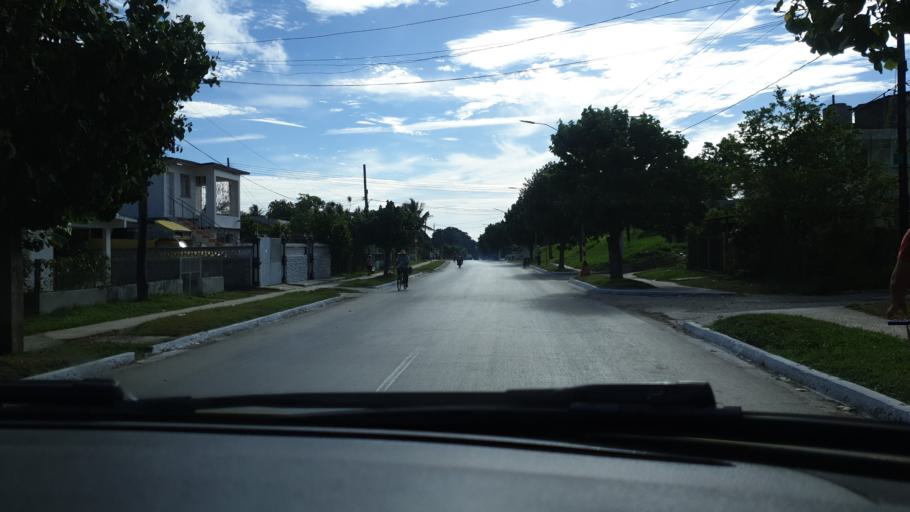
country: CU
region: Villa Clara
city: Santa Clara
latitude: 22.4136
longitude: -79.9513
